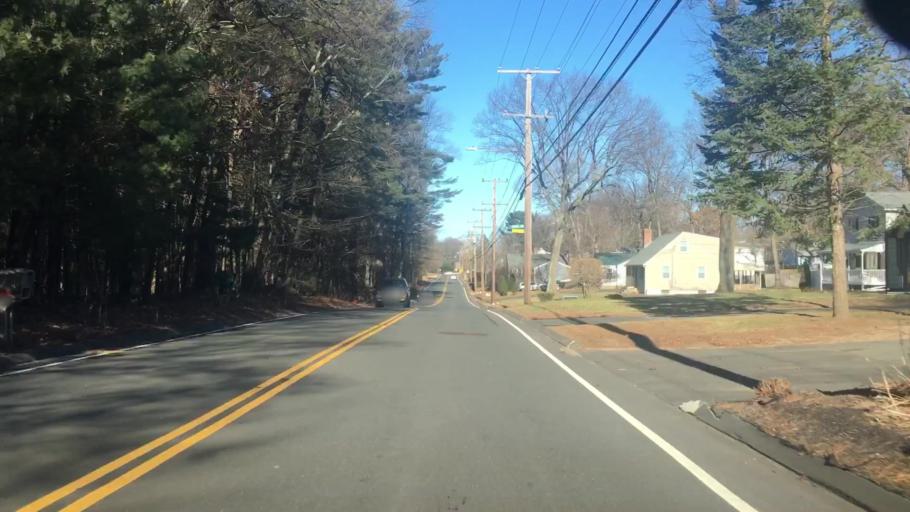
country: US
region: Connecticut
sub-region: Hartford County
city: Plainville
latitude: 41.6639
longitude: -72.9019
